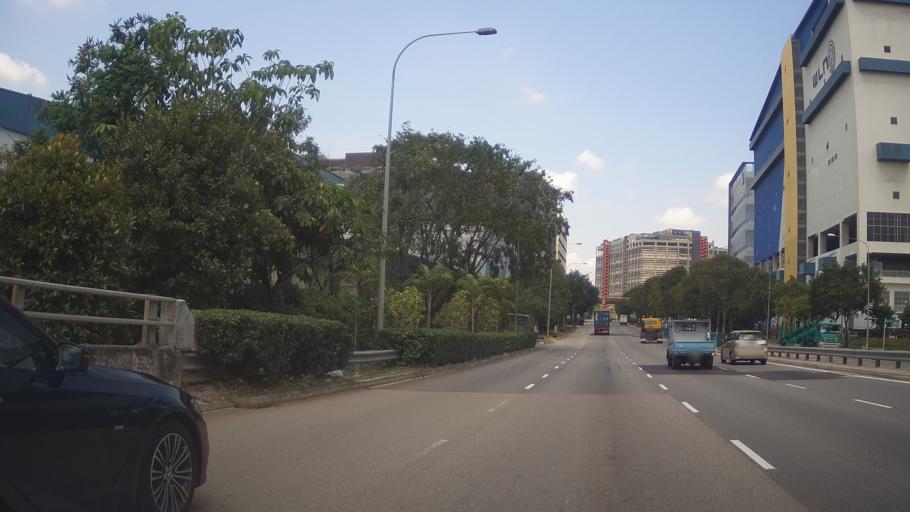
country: SG
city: Singapore
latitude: 1.3131
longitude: 103.7253
